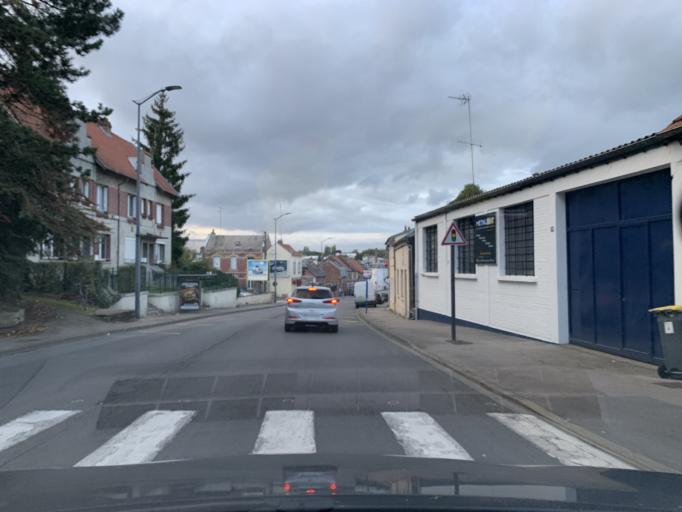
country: FR
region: Picardie
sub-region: Departement de l'Aisne
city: Saint-Quentin
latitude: 49.8552
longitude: 3.2799
